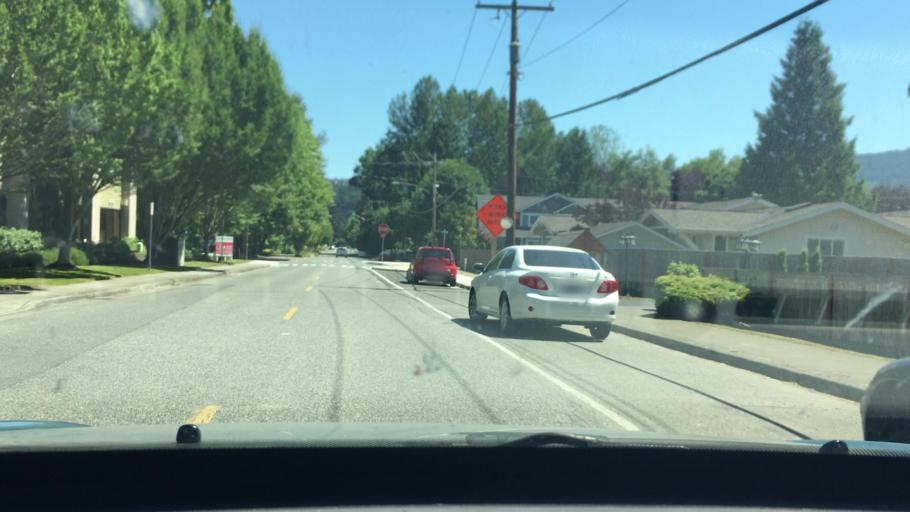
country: US
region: Washington
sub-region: King County
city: Issaquah
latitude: 47.5389
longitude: -122.0480
